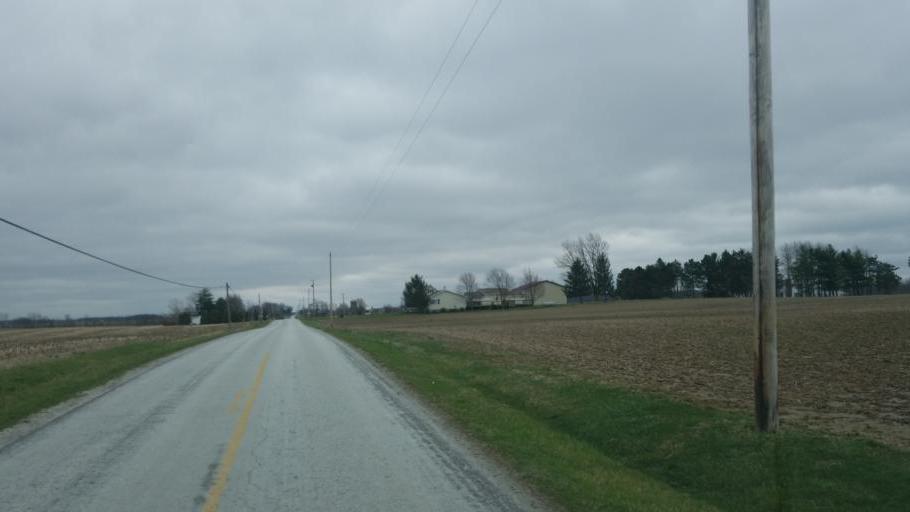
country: US
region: Ohio
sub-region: Hardin County
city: Kenton
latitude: 40.6588
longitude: -83.5646
